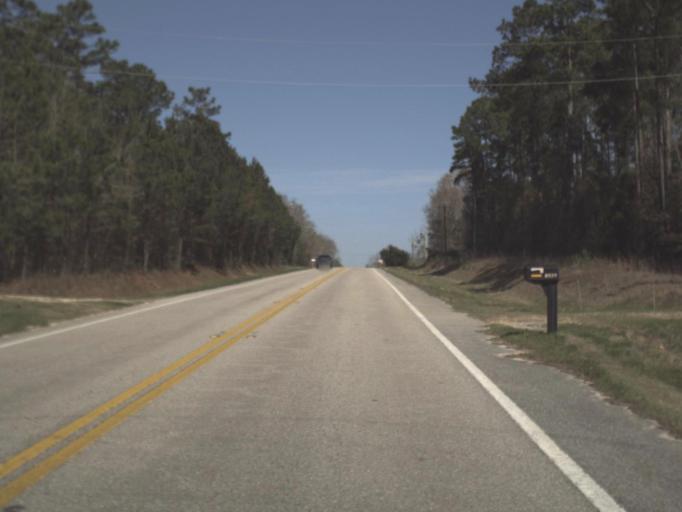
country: US
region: Florida
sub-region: Jefferson County
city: Monticello
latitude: 30.3963
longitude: -84.0157
